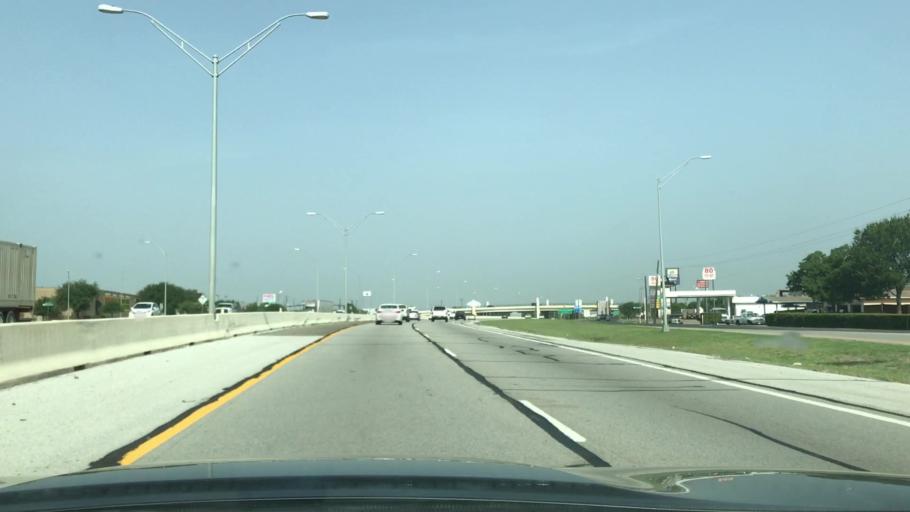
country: US
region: Texas
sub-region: Dallas County
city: Mesquite
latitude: 32.7925
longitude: -96.6507
